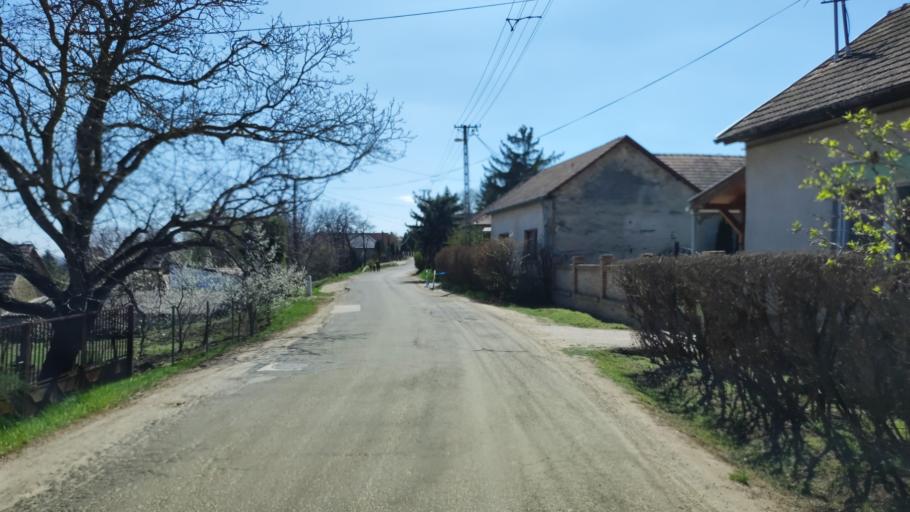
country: HU
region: Pest
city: Kosd
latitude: 47.8059
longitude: 19.1771
